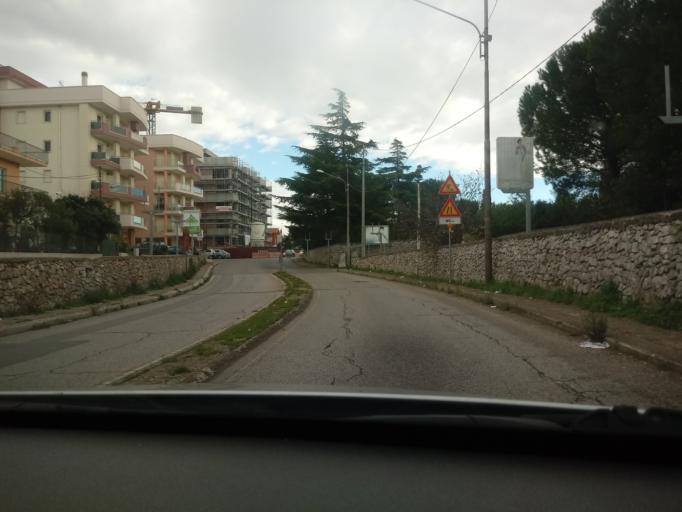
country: IT
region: Apulia
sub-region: Provincia di Bari
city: Putignano
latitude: 40.8558
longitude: 17.1114
